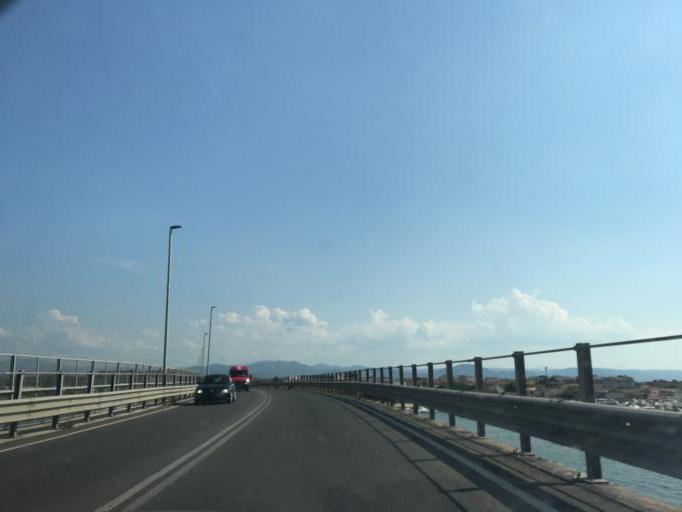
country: IT
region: Sardinia
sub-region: Provincia di Olbia-Tempio
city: Olbia
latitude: 40.9201
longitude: 9.5014
